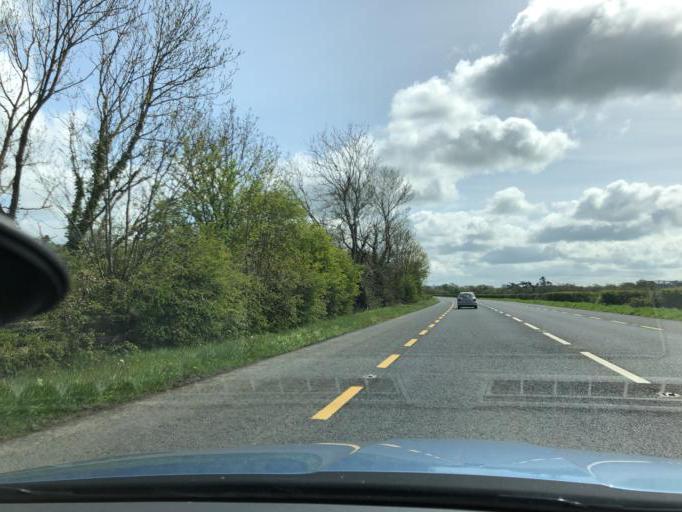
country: IE
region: Munster
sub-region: County Cork
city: Kanturk
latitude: 52.1248
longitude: -8.7919
